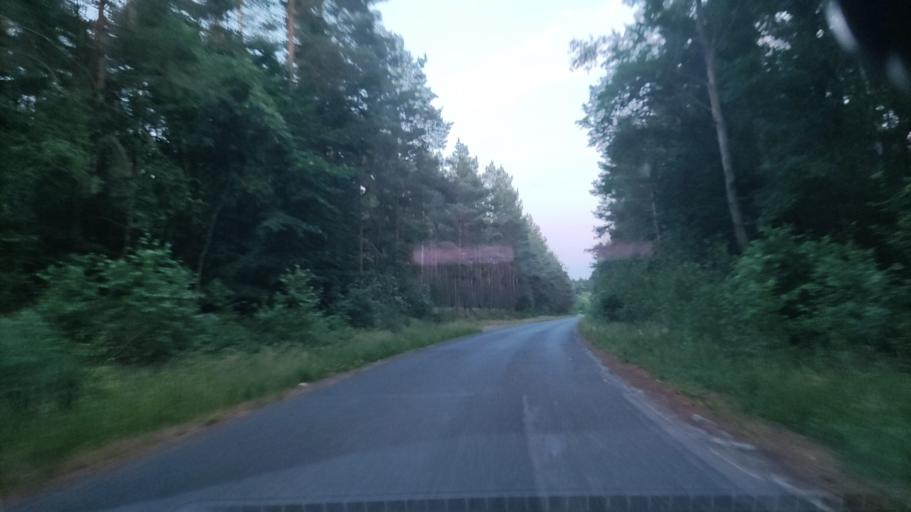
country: DE
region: Lower Saxony
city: Soderstorf
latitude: 53.1311
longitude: 10.1148
